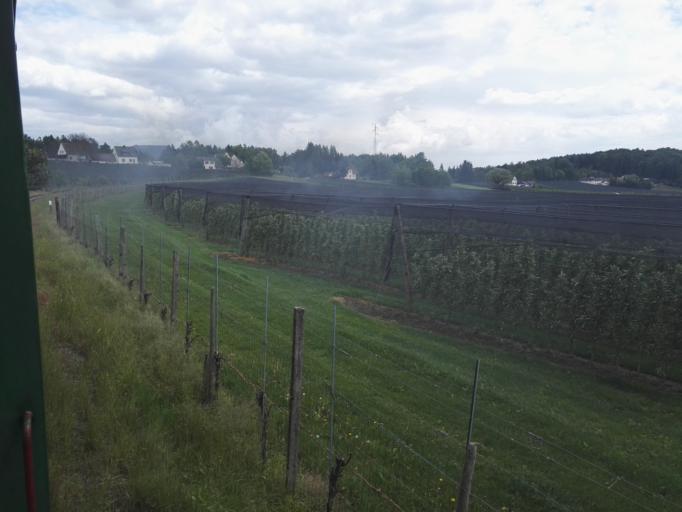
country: AT
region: Styria
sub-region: Politischer Bezirk Weiz
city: Krottendorf
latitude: 47.2181
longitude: 15.6532
